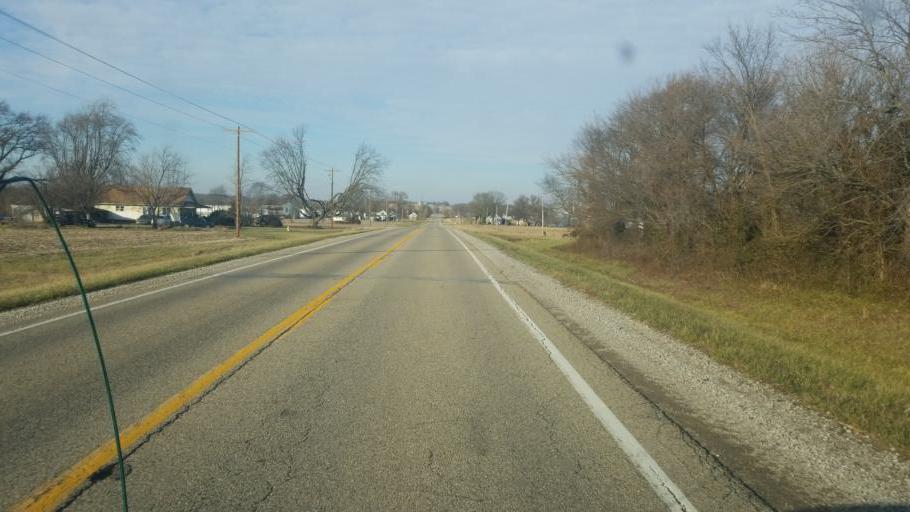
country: US
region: Illinois
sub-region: Lawrence County
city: Lawrenceville
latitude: 38.6295
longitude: -87.6939
